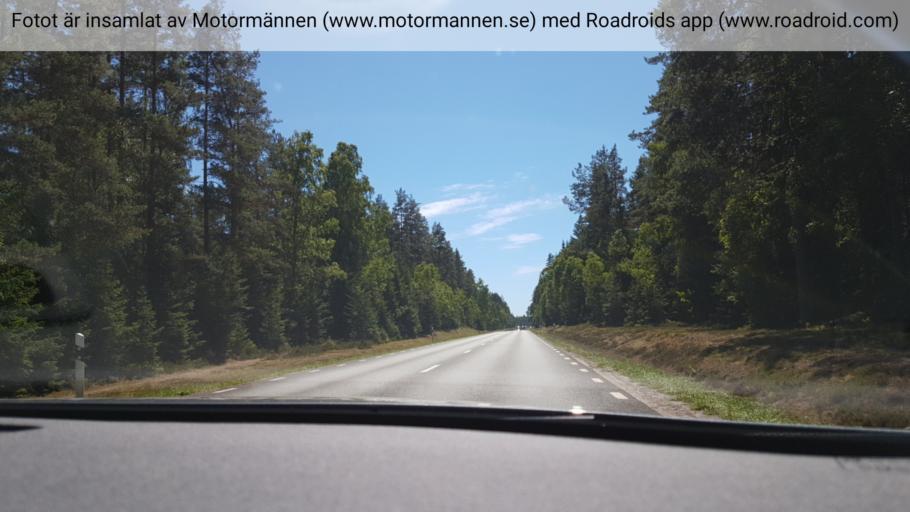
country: SE
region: Joenkoeping
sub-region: Gnosjo Kommun
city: Gnosjoe
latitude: 57.4334
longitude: 13.6202
